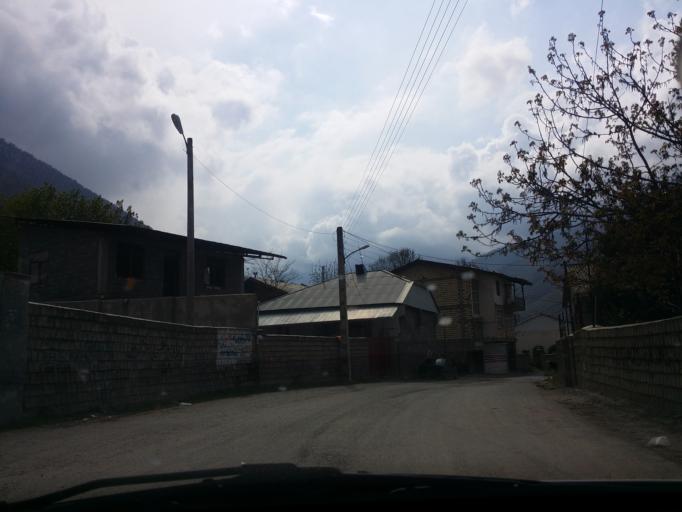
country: IR
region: Mazandaran
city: `Abbasabad
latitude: 36.4827
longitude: 51.1386
